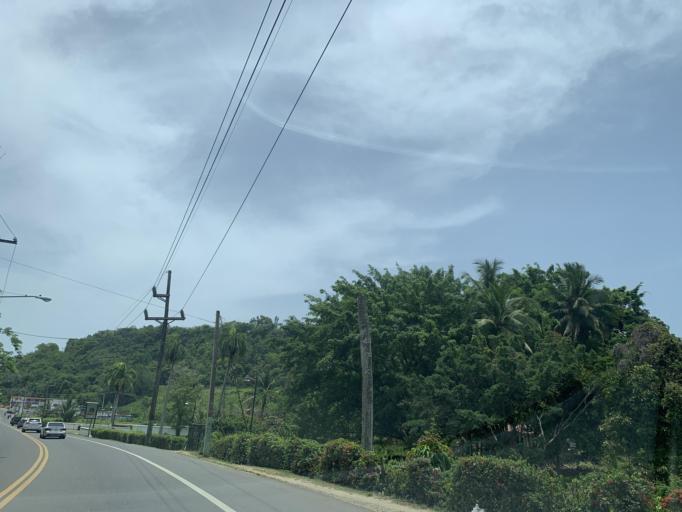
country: DO
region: Puerto Plata
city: Cabarete
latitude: 19.7463
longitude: -70.5200
